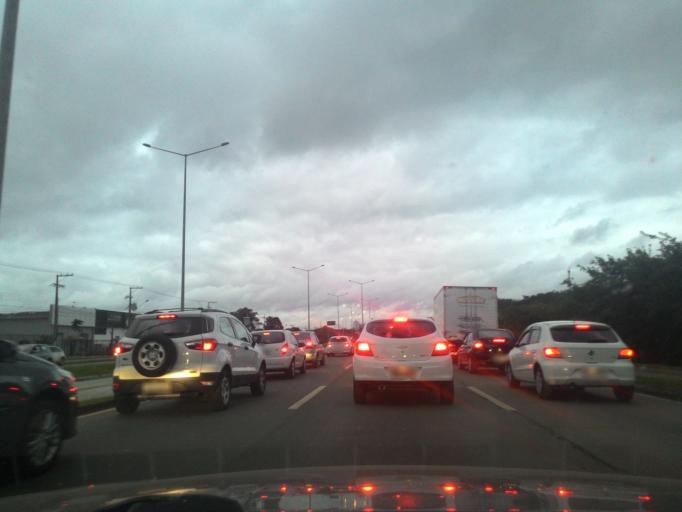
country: BR
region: Parana
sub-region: Curitiba
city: Curitiba
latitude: -25.4635
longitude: -49.2514
